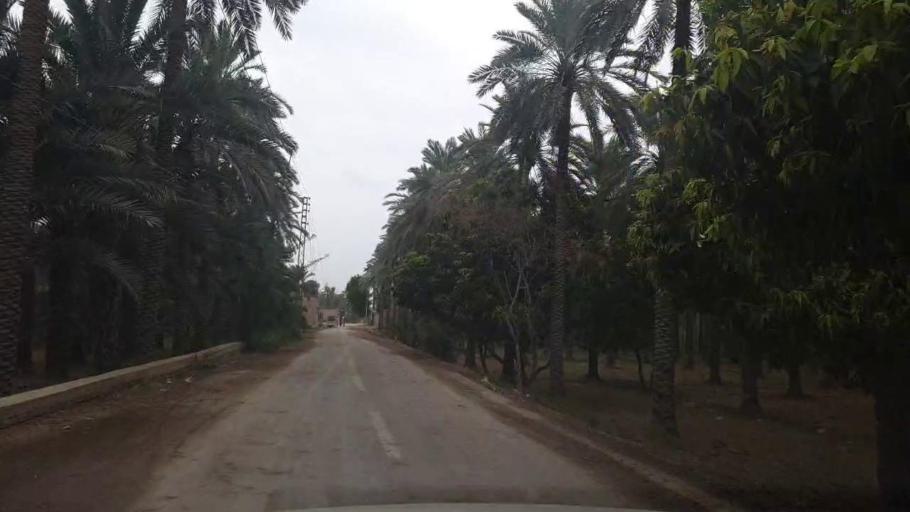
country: PK
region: Sindh
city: Khairpur
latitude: 27.5480
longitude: 68.7511
